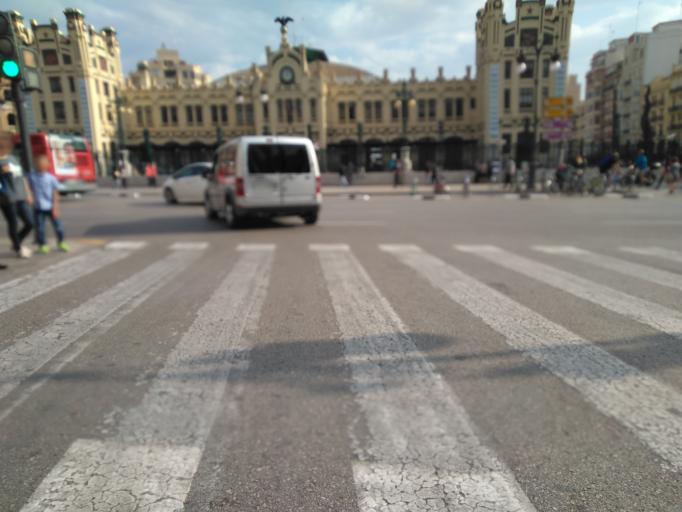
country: ES
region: Valencia
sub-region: Provincia de Valencia
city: Valencia
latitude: 39.4677
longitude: -0.3771
